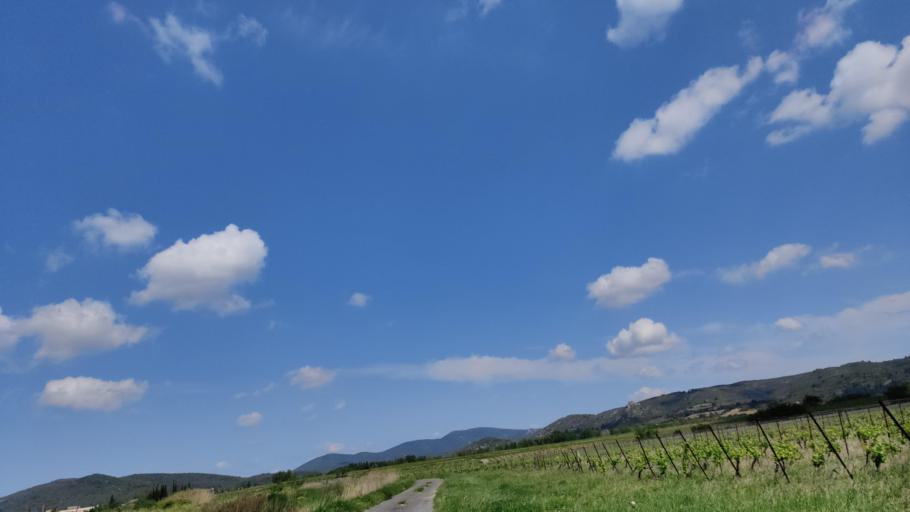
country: FR
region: Languedoc-Roussillon
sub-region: Departement des Pyrenees-Orientales
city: Estagel
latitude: 42.8796
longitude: 2.7203
